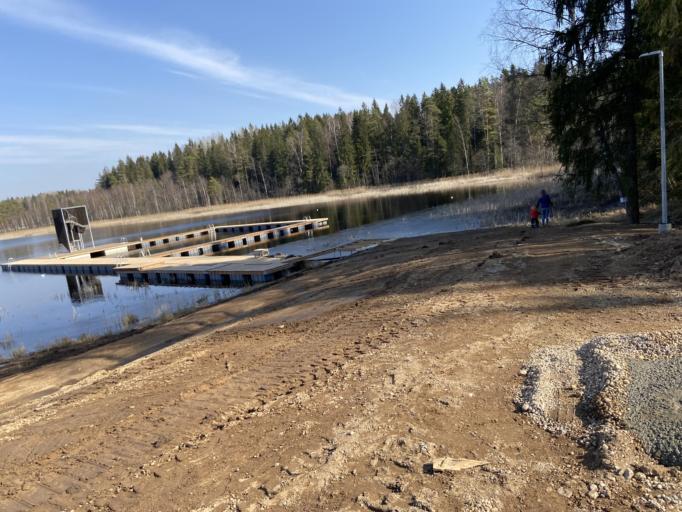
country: EE
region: Vorumaa
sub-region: Antsla vald
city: Vana-Antsla
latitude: 58.0007
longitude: 26.3982
